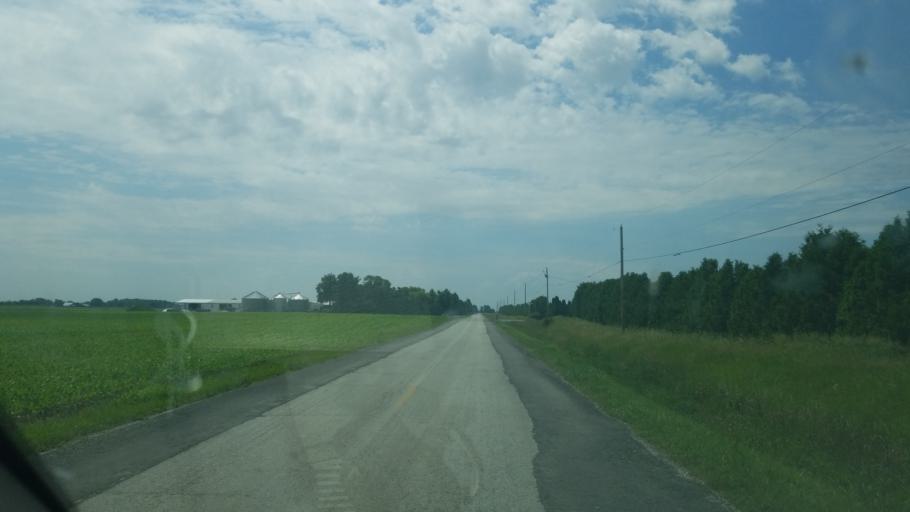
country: US
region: Ohio
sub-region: Wood County
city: North Baltimore
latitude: 41.2672
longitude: -83.5929
